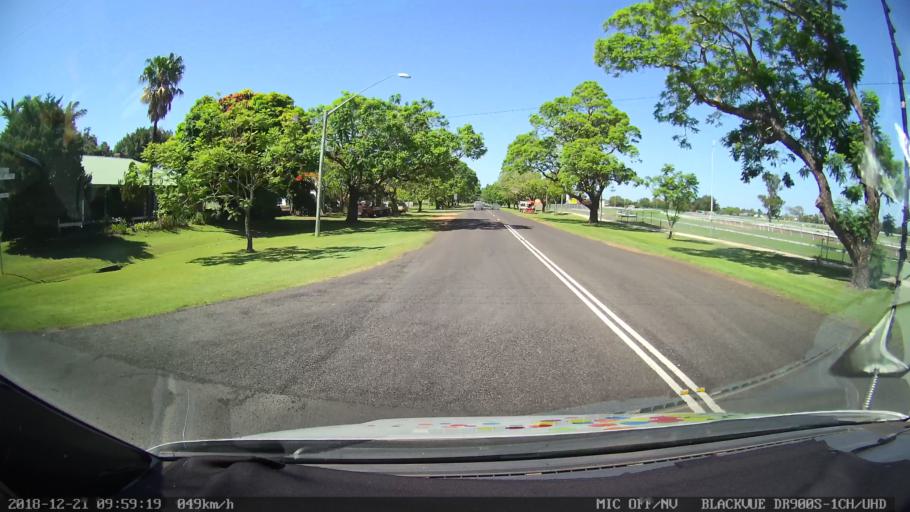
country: AU
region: New South Wales
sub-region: Clarence Valley
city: Grafton
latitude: -29.6775
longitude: 152.9314
